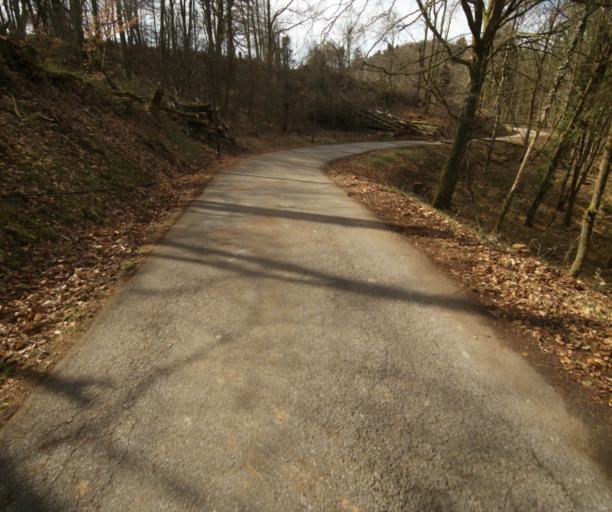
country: FR
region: Limousin
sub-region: Departement de la Correze
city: Correze
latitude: 45.3606
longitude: 1.8693
